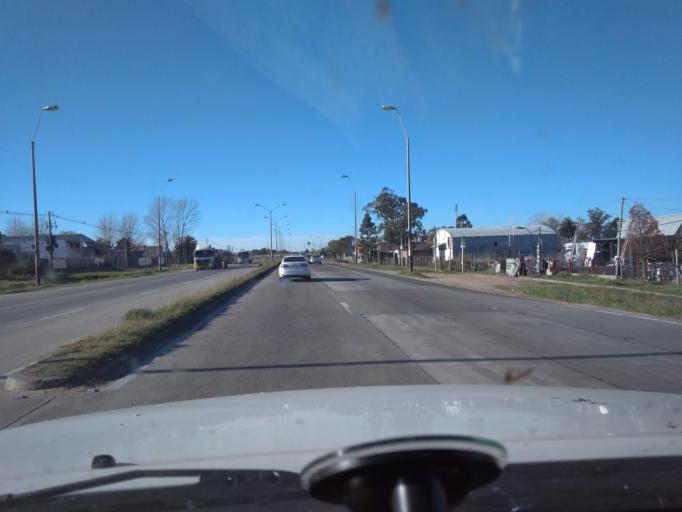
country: UY
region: Canelones
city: Colonia Nicolich
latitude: -34.7784
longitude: -56.0559
